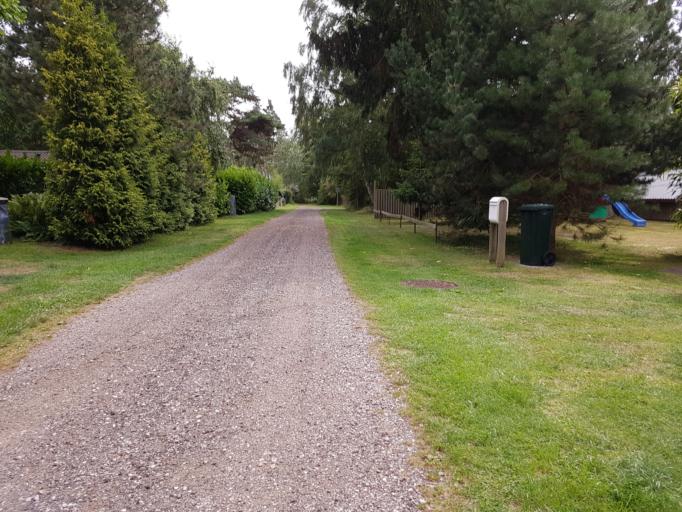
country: DK
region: Zealand
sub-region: Guldborgsund Kommune
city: Nykobing Falster
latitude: 54.5923
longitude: 11.9686
